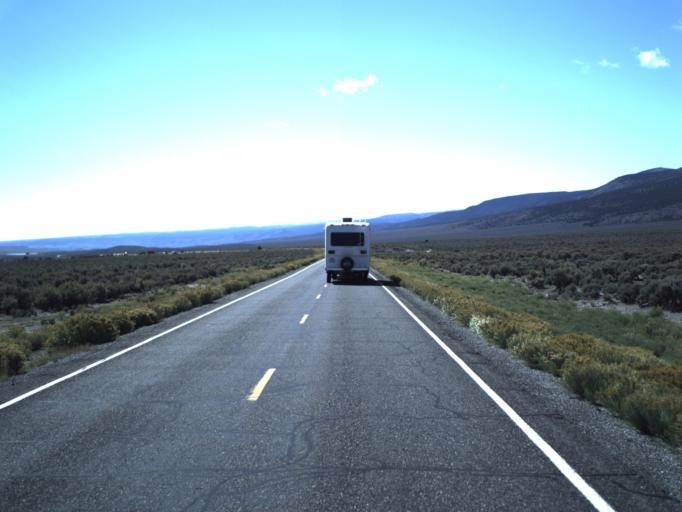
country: US
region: Utah
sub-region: Piute County
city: Junction
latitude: 38.2769
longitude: -111.9840
